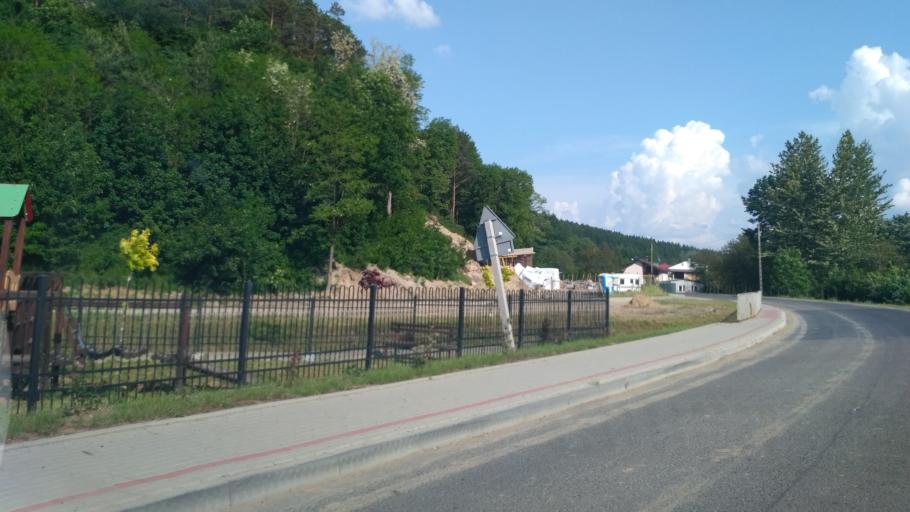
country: PL
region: Subcarpathian Voivodeship
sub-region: Powiat jaroslawski
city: Kramarzowka
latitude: 49.8850
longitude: 22.4971
